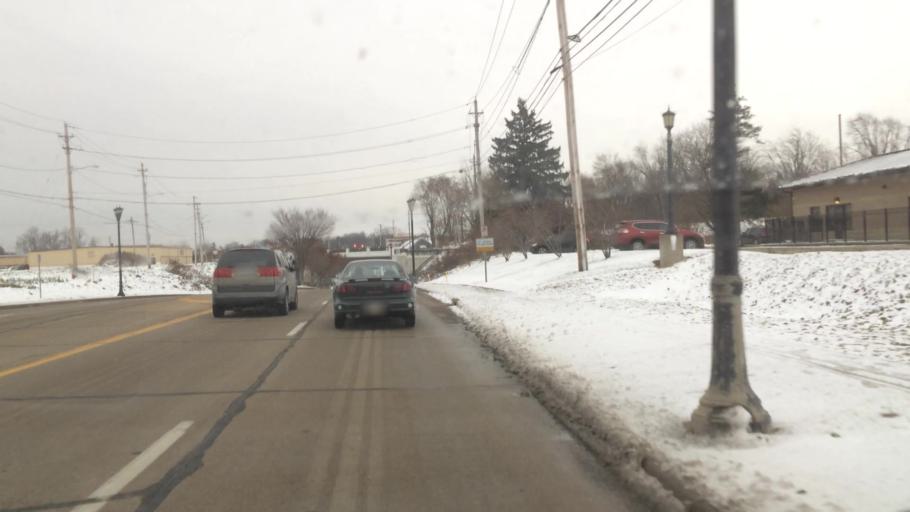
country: US
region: Ohio
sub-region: Cuyahoga County
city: Berea
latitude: 41.3723
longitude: -81.8744
